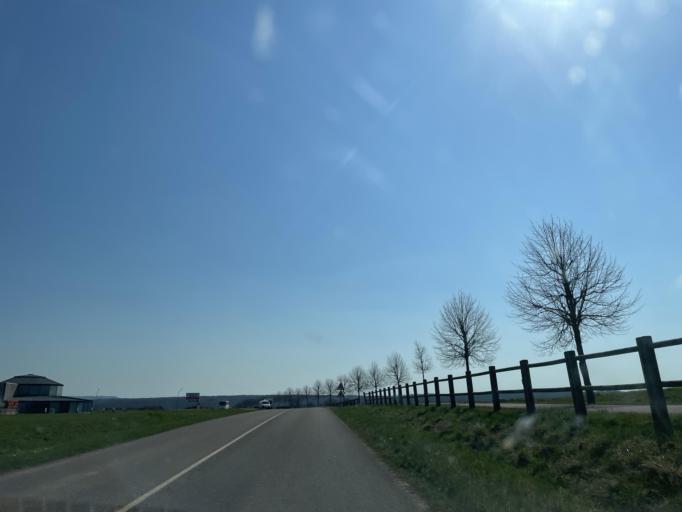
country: FR
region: Bourgogne
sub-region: Departement de la Cote-d'Or
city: Semur-en-Auxois
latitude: 47.4820
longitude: 4.3480
